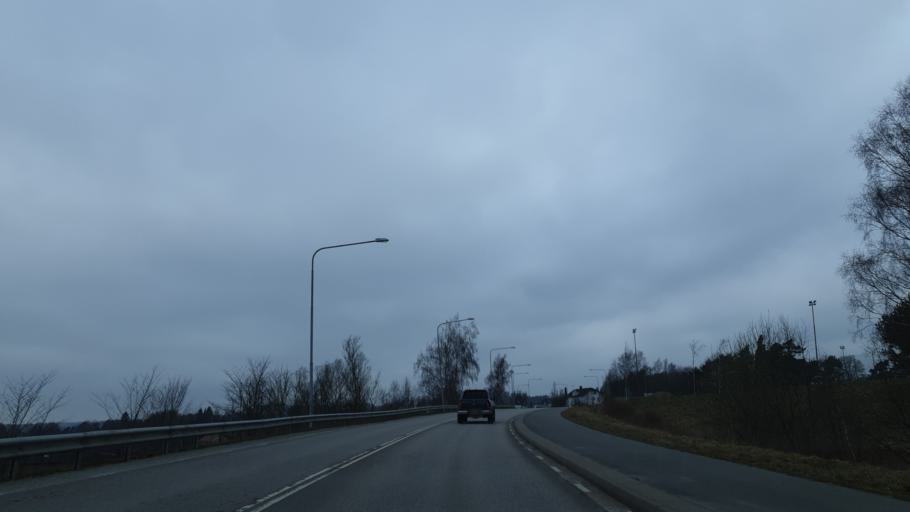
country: SE
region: Vaestra Goetaland
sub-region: Marks Kommun
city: Kinna
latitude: 57.5043
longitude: 12.6904
